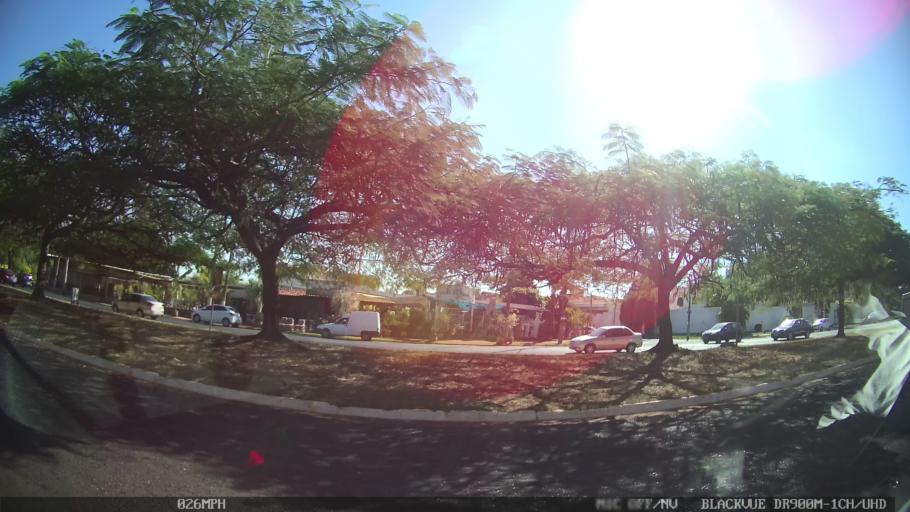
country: BR
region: Sao Paulo
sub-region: Ribeirao Preto
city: Ribeirao Preto
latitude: -21.2037
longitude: -47.7683
